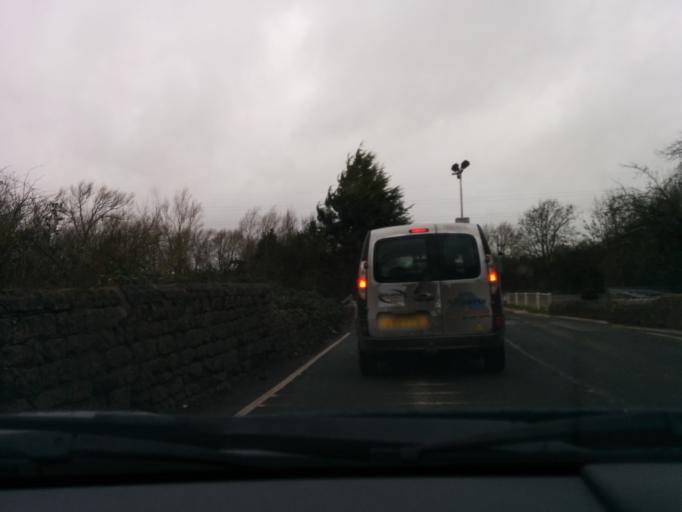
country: GB
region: England
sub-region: Oxfordshire
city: Eynsham
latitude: 51.7748
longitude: -1.3597
